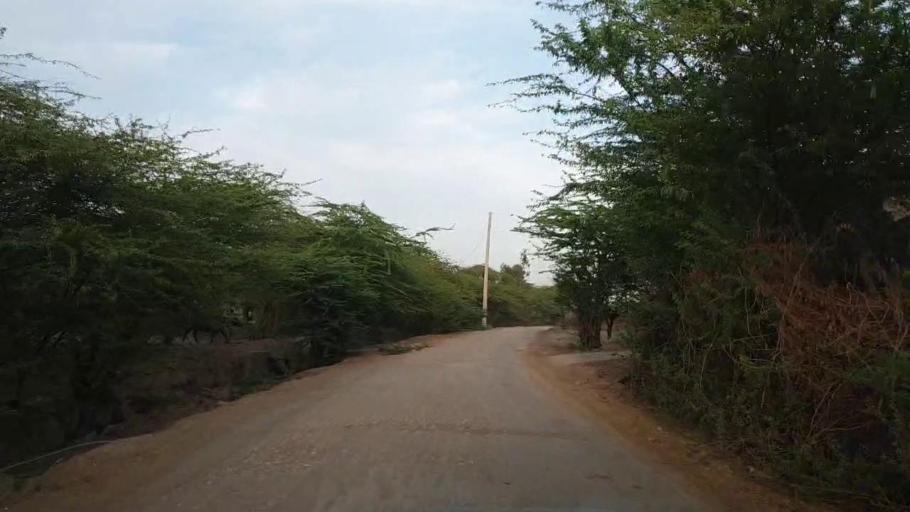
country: PK
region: Sindh
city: Kunri
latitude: 25.1605
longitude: 69.5558
